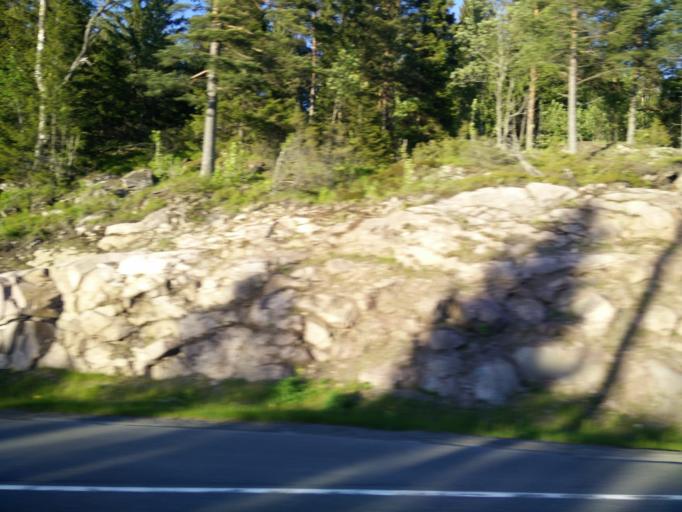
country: NO
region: Buskerud
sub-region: Hole
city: Vik
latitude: 59.9731
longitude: 10.3334
